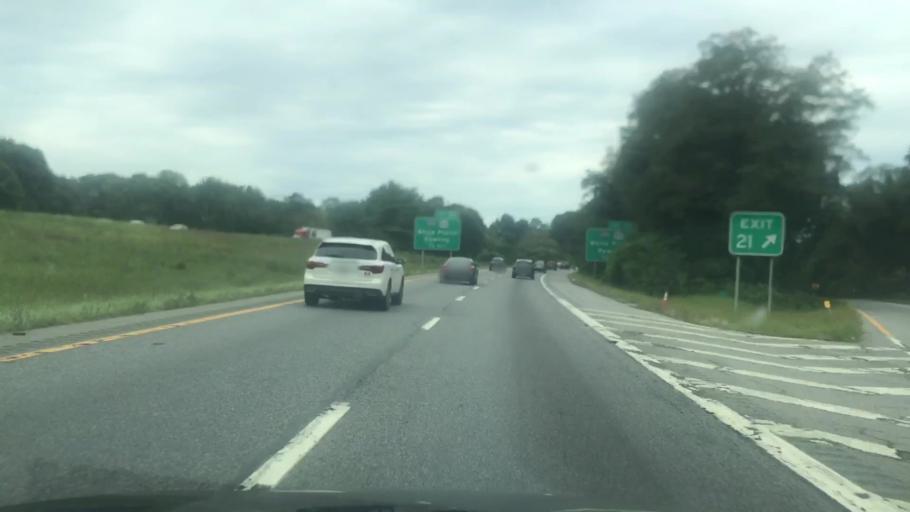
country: US
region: New York
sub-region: Putnam County
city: Peach Lake
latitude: 41.3839
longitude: -73.5763
